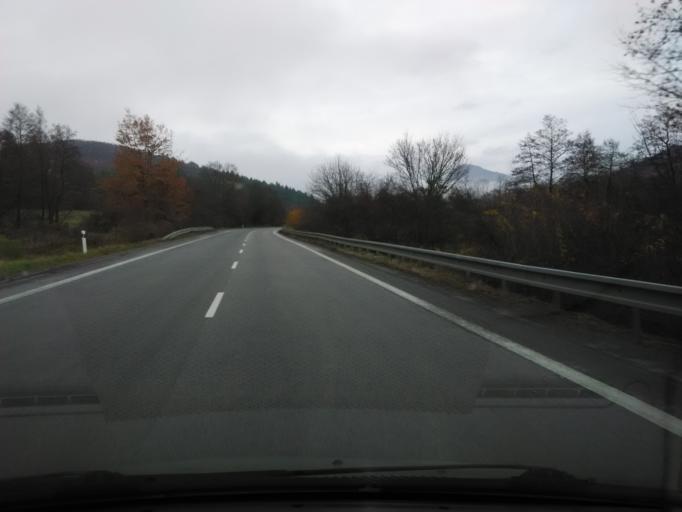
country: SK
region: Banskobystricky
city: Ziar nad Hronom
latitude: 48.6137
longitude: 18.8926
